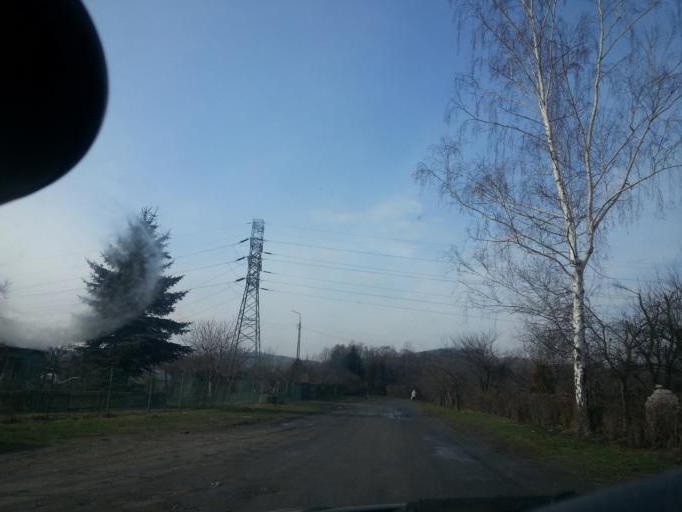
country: PL
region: Lower Silesian Voivodeship
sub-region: Powiat jeleniogorski
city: Jezow Sudecki
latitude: 50.9179
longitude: 15.7448
